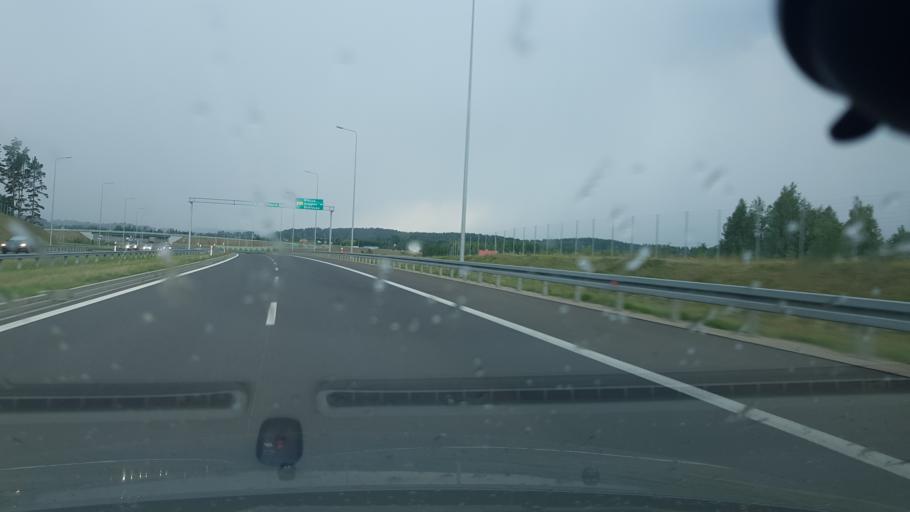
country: PL
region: Warmian-Masurian Voivodeship
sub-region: Powiat nidzicki
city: Nidzica
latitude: 53.3681
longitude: 20.3882
